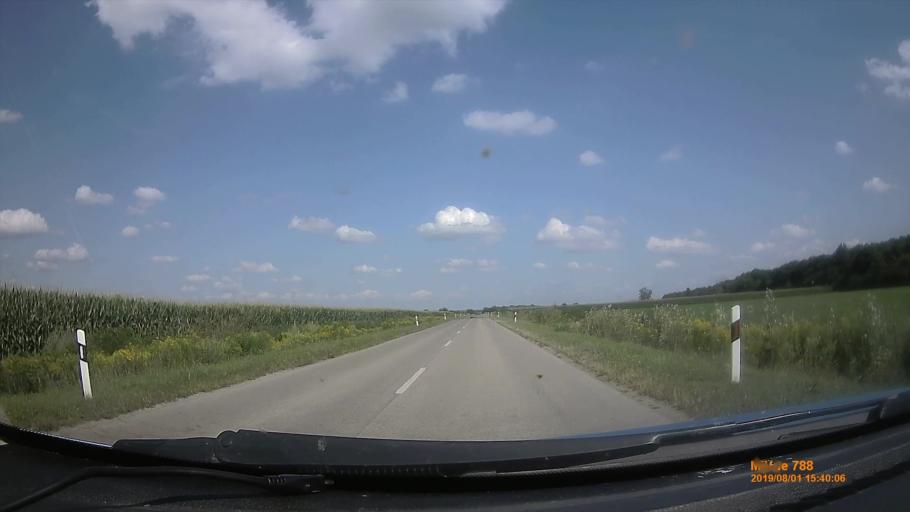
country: HU
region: Baranya
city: Szentlorinc
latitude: 45.9883
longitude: 17.9468
